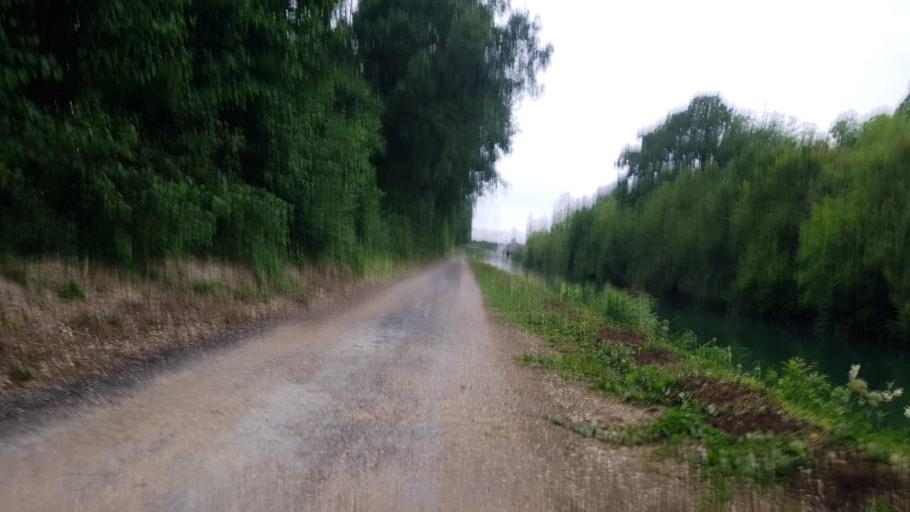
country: FR
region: Champagne-Ardenne
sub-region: Departement de la Marne
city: Sarry
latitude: 48.8431
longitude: 4.4974
